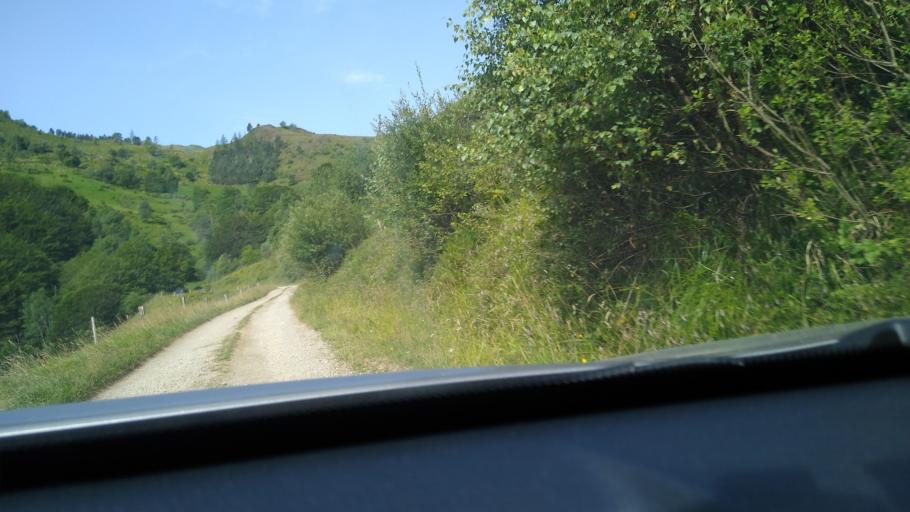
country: FR
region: Midi-Pyrenees
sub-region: Departement de l'Ariege
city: Saint-Girons
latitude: 42.7914
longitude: 1.1497
